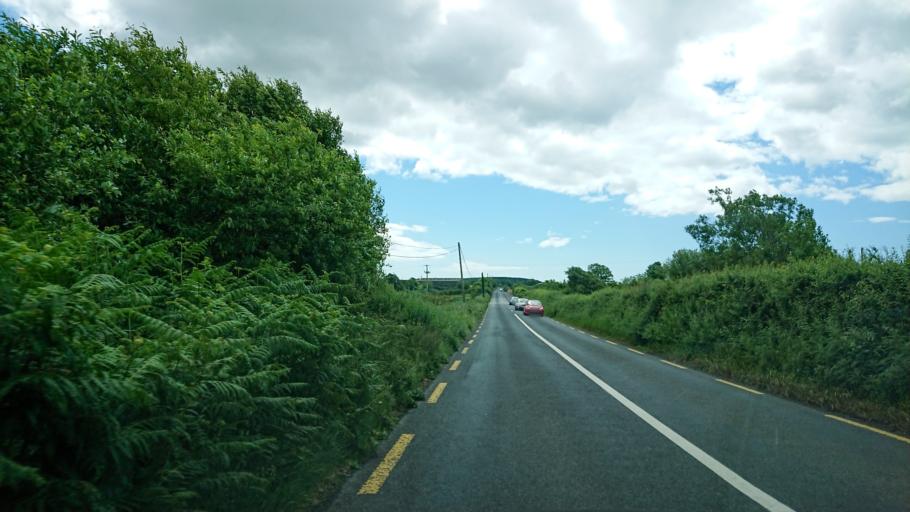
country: IE
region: Munster
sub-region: Waterford
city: Tra Mhor
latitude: 52.1959
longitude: -7.1908
